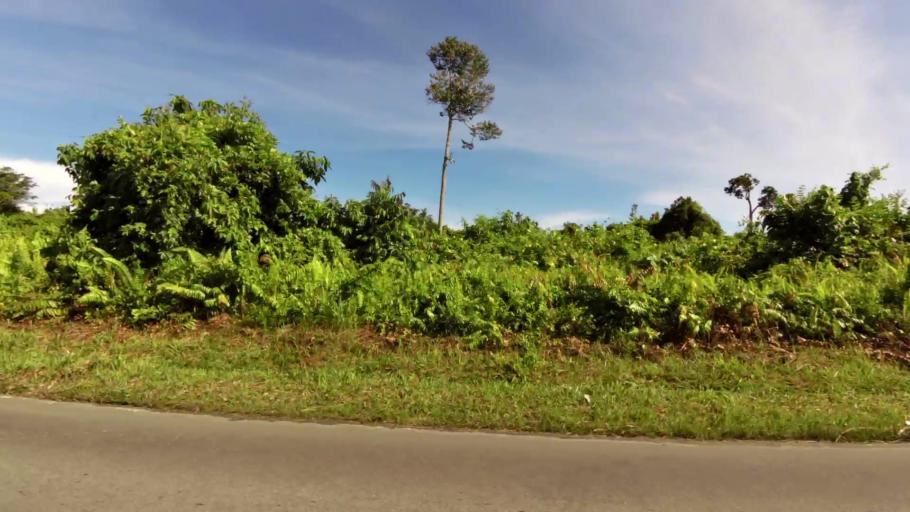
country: BN
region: Belait
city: Kuala Belait
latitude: 4.5859
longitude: 114.2165
